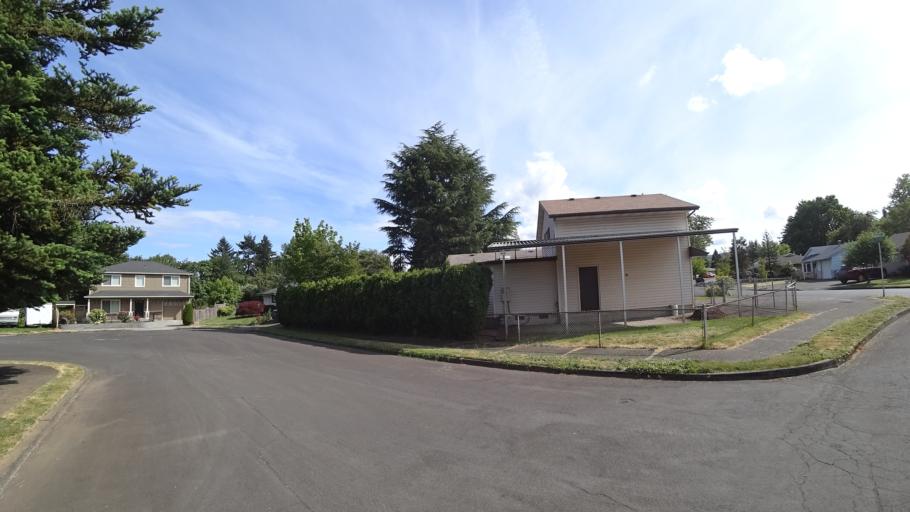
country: US
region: Oregon
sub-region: Washington County
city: West Haven
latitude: 45.5900
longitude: -122.7332
